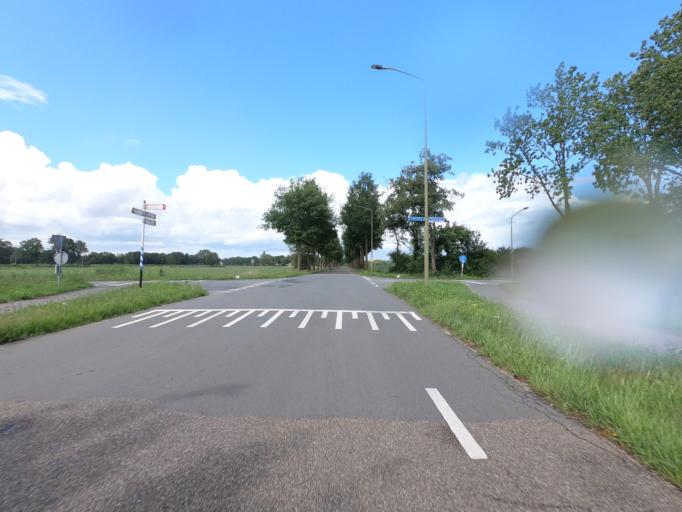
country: NL
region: North Brabant
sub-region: Gemeente Landerd
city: Zeeland
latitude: 51.7129
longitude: 5.6848
